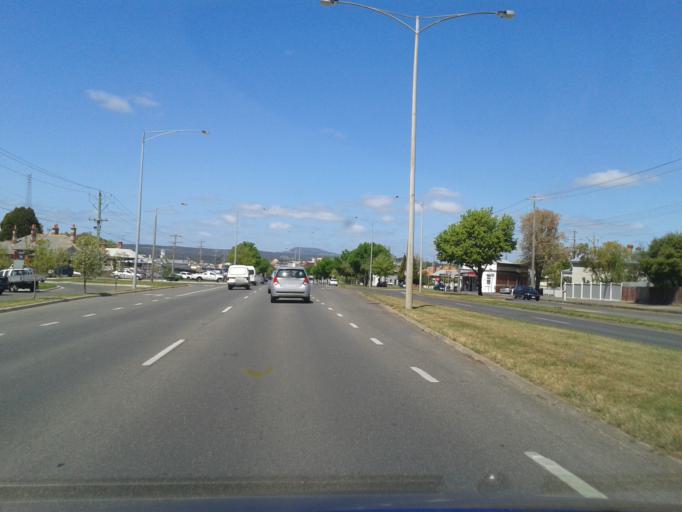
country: AU
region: Victoria
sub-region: Ballarat North
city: Lake Wendouree
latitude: -37.5515
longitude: 143.8512
